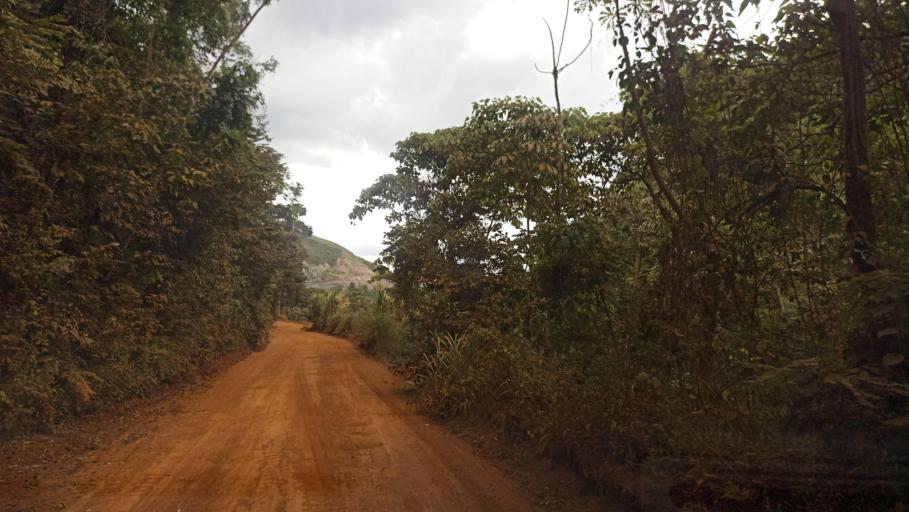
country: BR
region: Minas Gerais
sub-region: Congonhas
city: Congonhas
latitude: -20.4283
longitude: -43.7726
